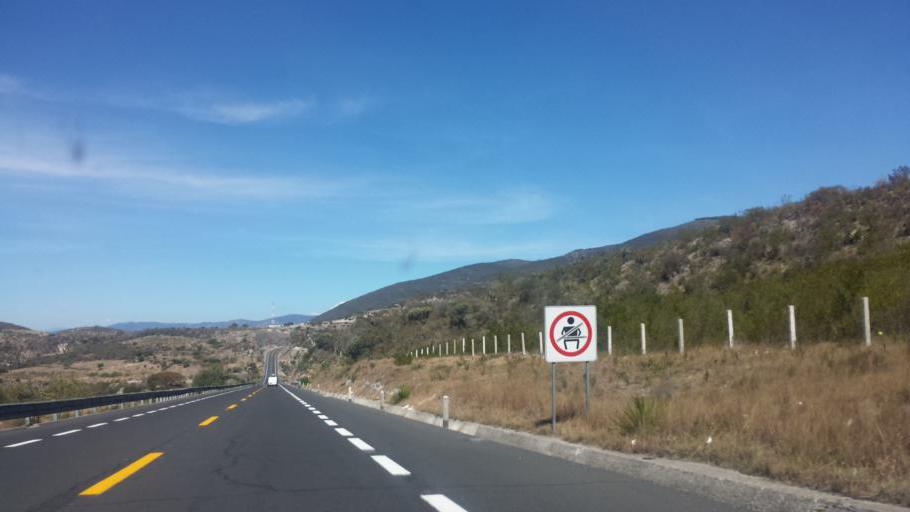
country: MX
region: Oaxaca
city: San Gabriel Casa Blanca
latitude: 17.9663
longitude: -97.3575
